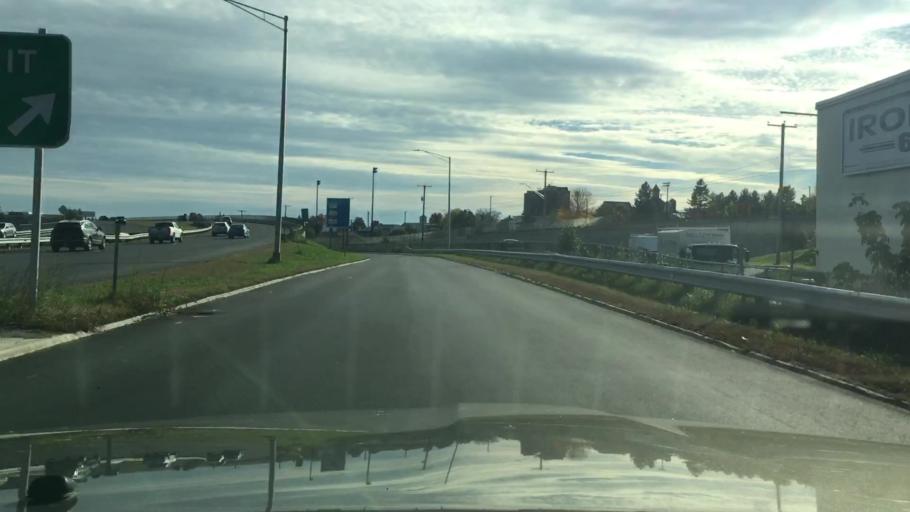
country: US
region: New Hampshire
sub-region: Hillsborough County
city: Manchester
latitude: 42.9884
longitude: -71.4719
